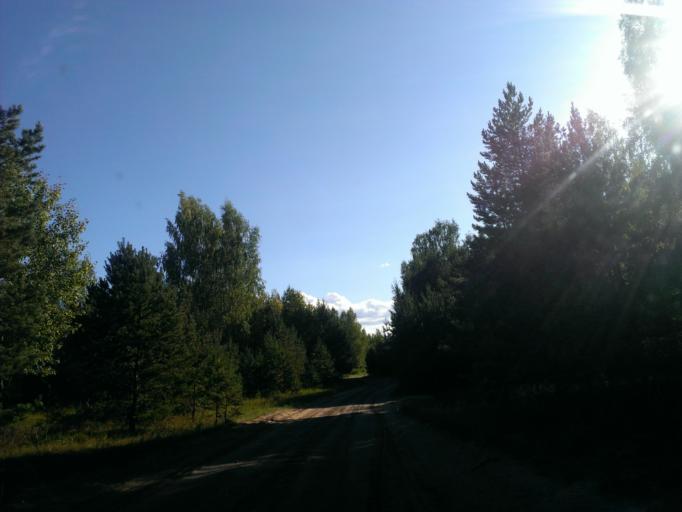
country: LV
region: Adazi
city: Adazi
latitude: 57.0600
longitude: 24.2599
